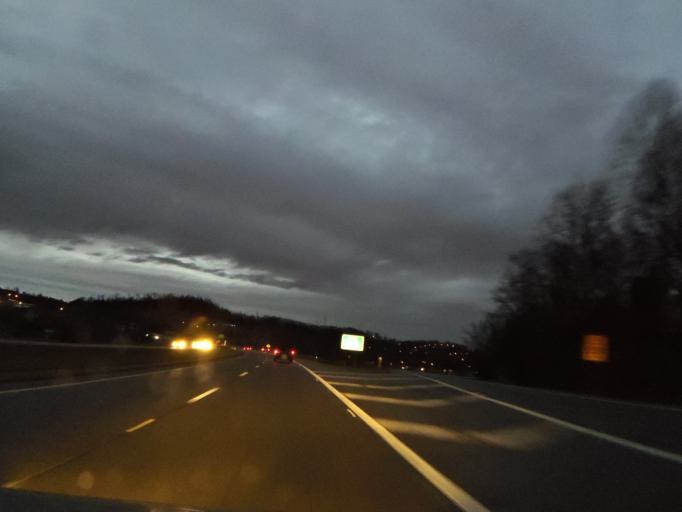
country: US
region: Tennessee
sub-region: Sullivan County
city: Colonial Heights
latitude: 36.4510
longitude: -82.5214
